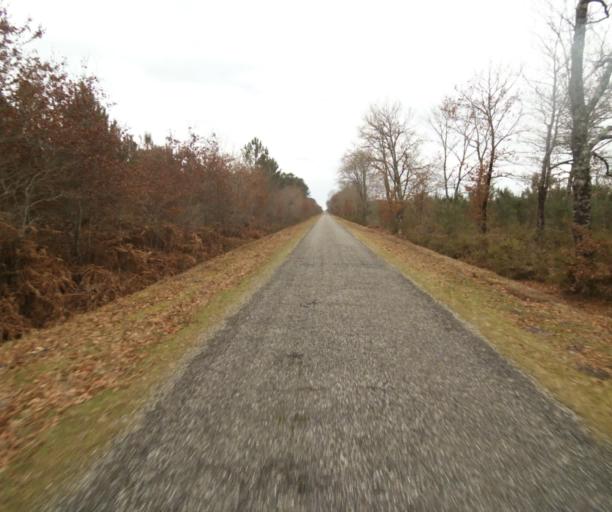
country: FR
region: Aquitaine
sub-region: Departement des Landes
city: Gabarret
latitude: 44.0199
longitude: -0.0432
